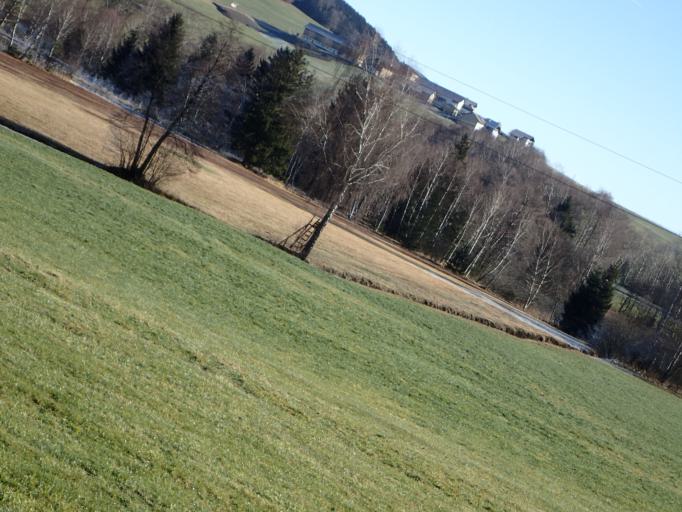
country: AT
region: Salzburg
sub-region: Politischer Bezirk Salzburg-Umgebung
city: Mattsee
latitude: 47.9641
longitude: 13.1210
